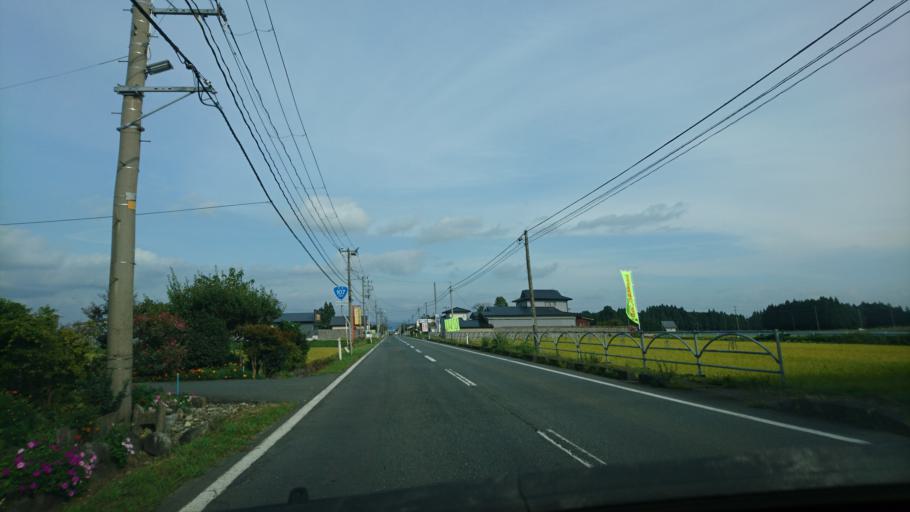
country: JP
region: Iwate
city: Kitakami
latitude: 39.3045
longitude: 141.0147
